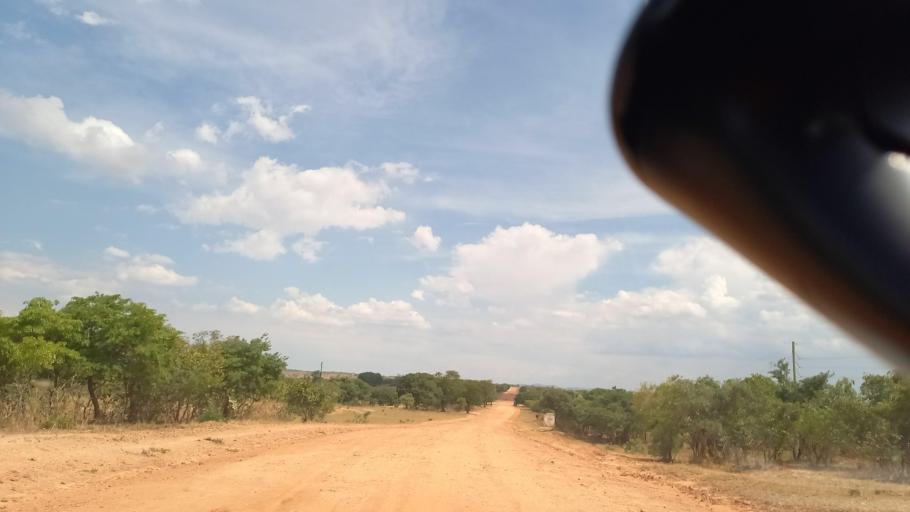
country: ZM
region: Lusaka
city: Kafue
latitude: -16.1312
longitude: 28.0479
